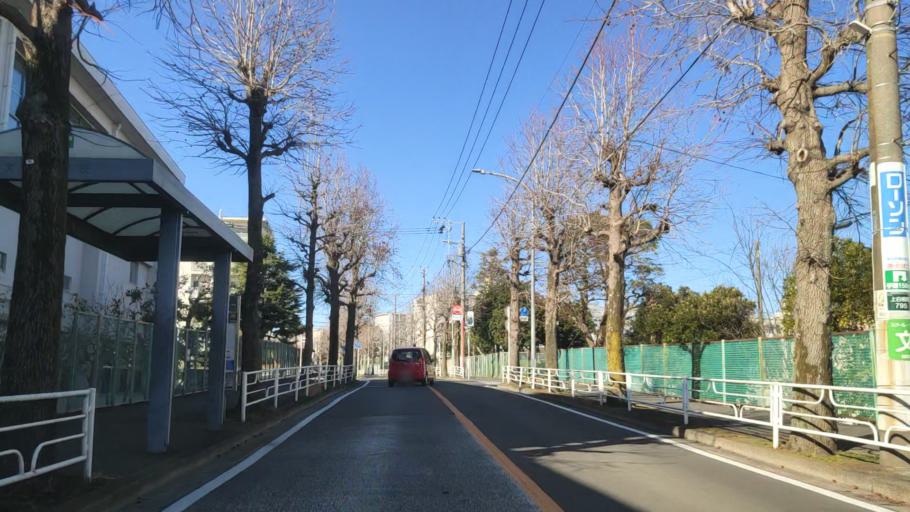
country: JP
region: Kanagawa
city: Minami-rinkan
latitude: 35.4966
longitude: 139.5325
